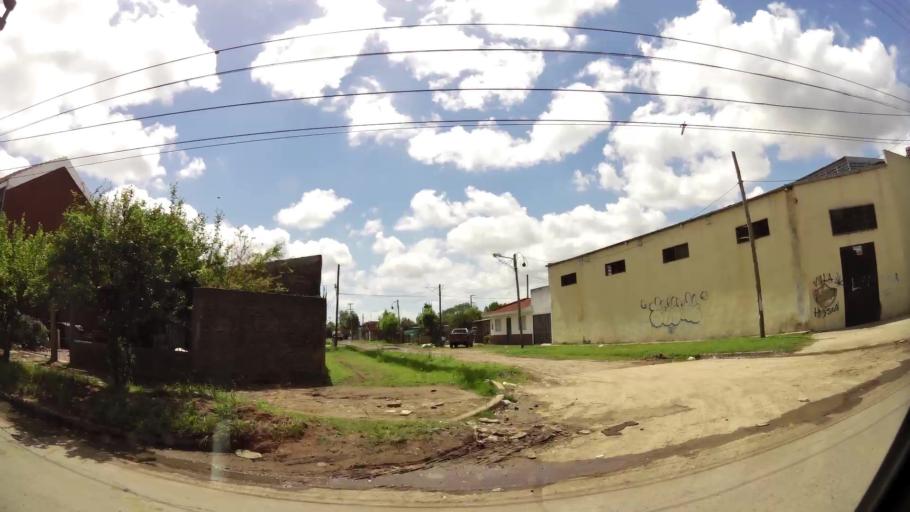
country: AR
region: Buenos Aires
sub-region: Partido de Quilmes
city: Quilmes
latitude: -34.8389
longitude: -58.2368
